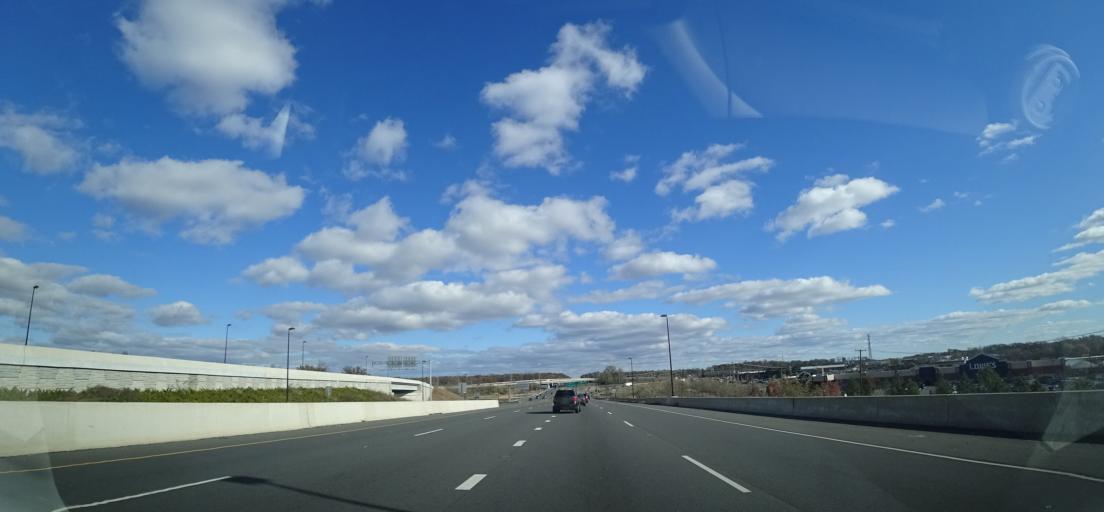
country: US
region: Virginia
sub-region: Prince William County
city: Gainesville
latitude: 38.7975
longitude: -77.6065
